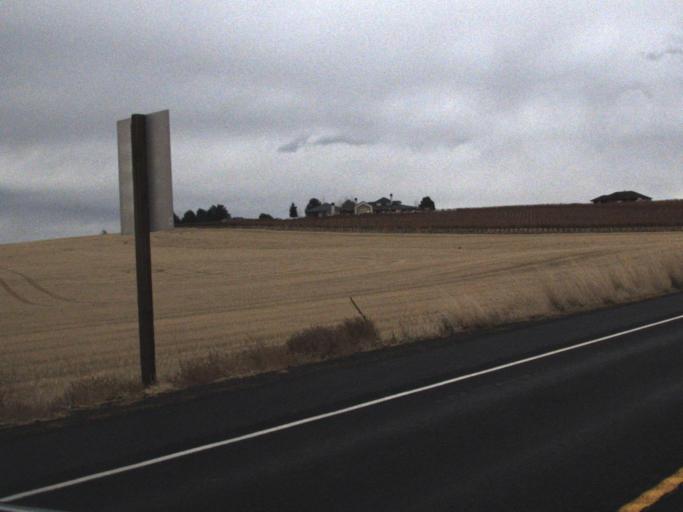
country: US
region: Washington
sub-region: Walla Walla County
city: Walla Walla East
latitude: 46.1027
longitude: -118.2436
